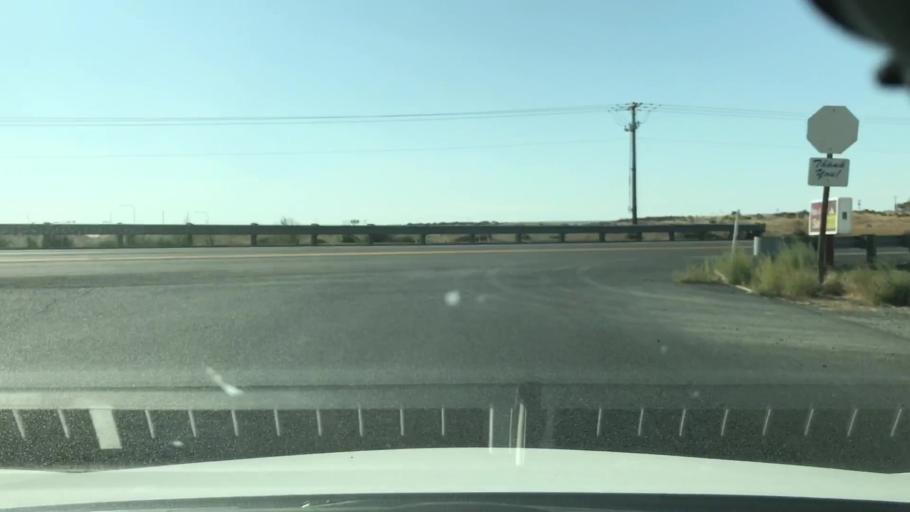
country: US
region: Washington
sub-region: Grant County
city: Moses Lake
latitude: 47.0996
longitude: -119.2356
